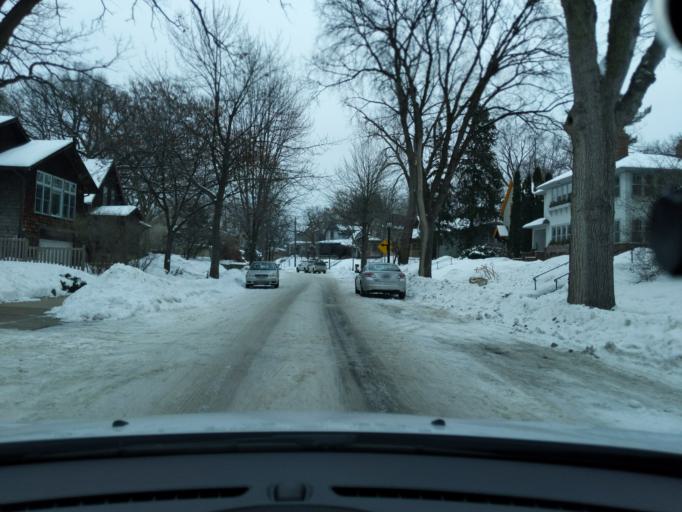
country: US
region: Minnesota
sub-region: Ramsey County
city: Lauderdale
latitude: 44.9655
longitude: -93.2113
